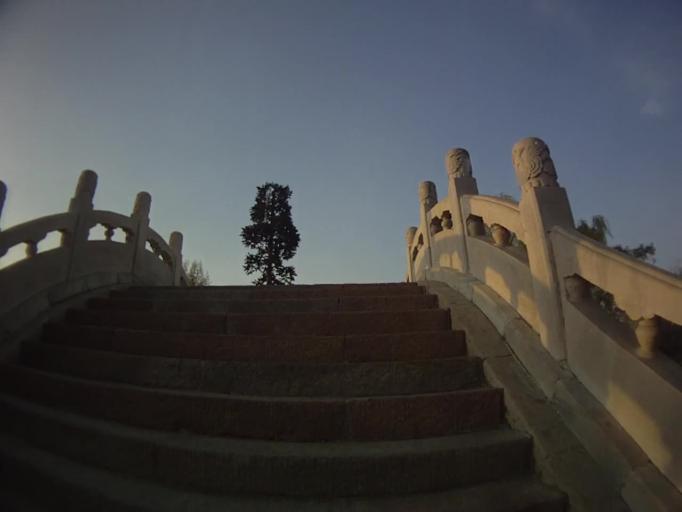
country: CN
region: Beijing
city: Longtan
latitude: 39.8792
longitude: 116.4331
